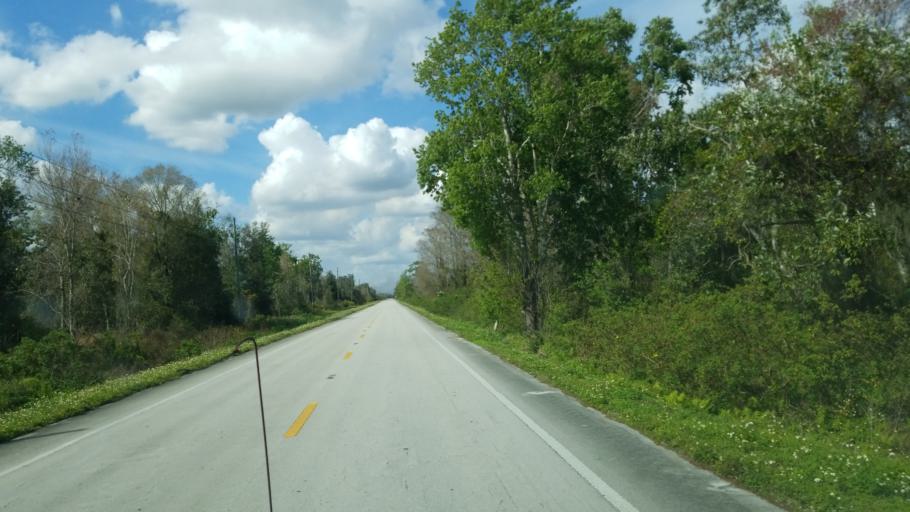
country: US
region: Florida
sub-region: Osceola County
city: Saint Cloud
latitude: 28.0083
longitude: -81.0256
